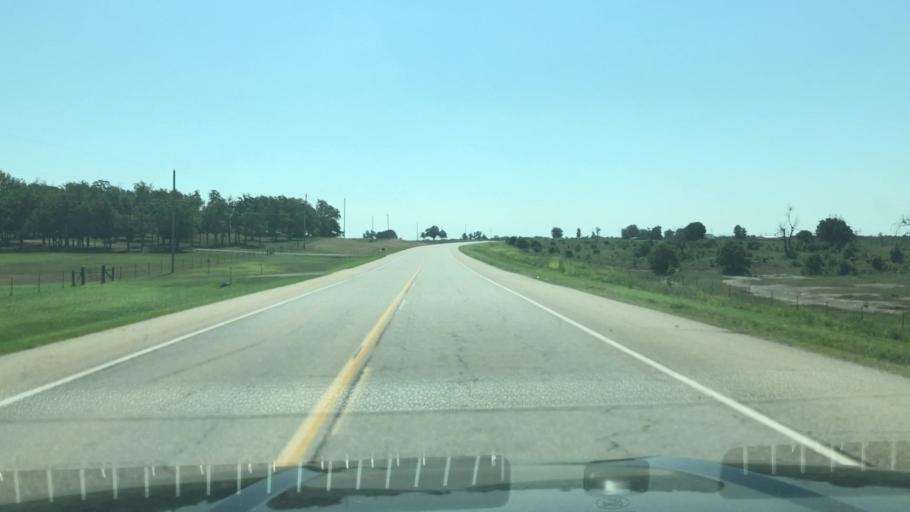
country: US
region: Oklahoma
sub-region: Creek County
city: Mannford
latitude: 35.9999
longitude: -96.3676
